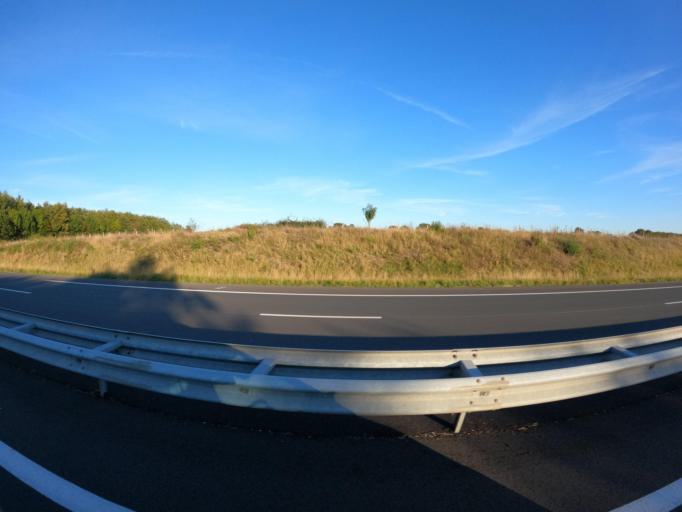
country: FR
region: Pays de la Loire
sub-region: Departement de la Vendee
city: Saint-Fulgent
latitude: 46.8554
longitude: -1.1434
